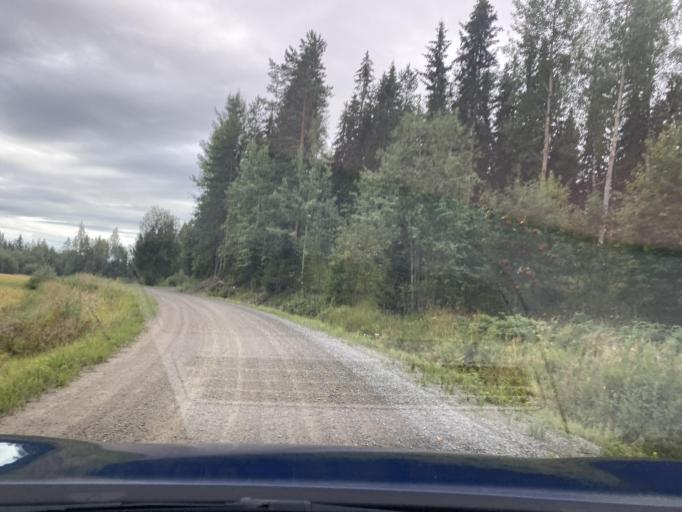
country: FI
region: Pirkanmaa
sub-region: Lounais-Pirkanmaa
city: Punkalaidun
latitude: 61.2445
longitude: 23.0447
